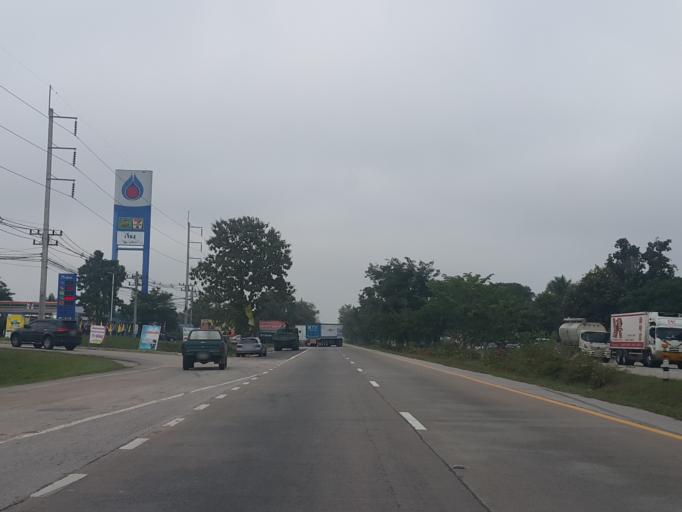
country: TH
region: Lampang
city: Hang Chat
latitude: 18.3186
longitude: 99.3553
